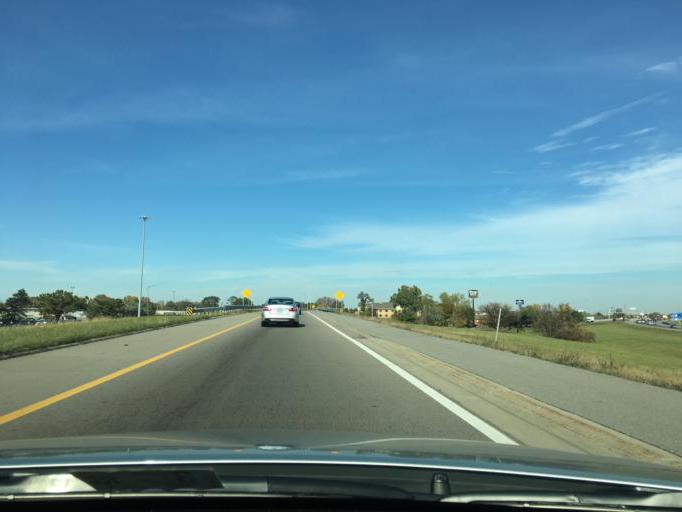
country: US
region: Michigan
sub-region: Macomb County
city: Roseville
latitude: 42.5204
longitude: -82.9166
